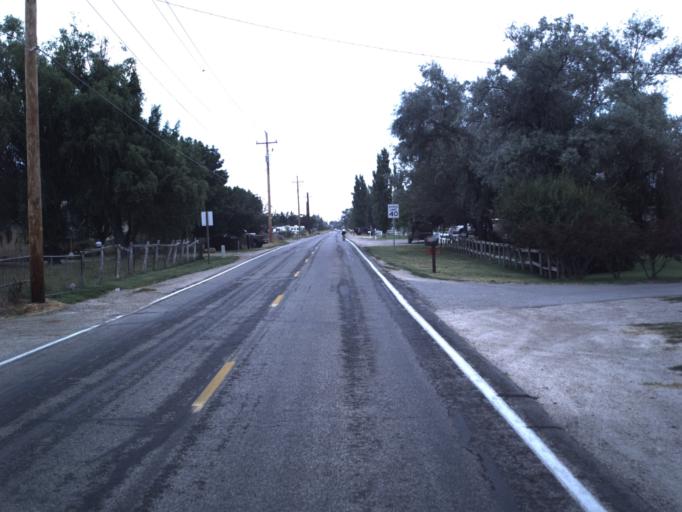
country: US
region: Utah
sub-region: Davis County
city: West Point
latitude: 41.1295
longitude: -112.1126
